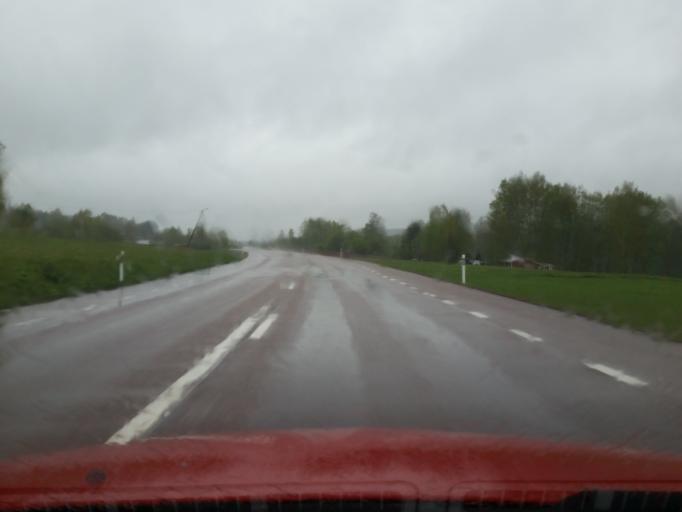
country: SE
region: Dalarna
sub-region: Gagnefs Kommun
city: Djuras
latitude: 60.5380
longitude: 15.2865
